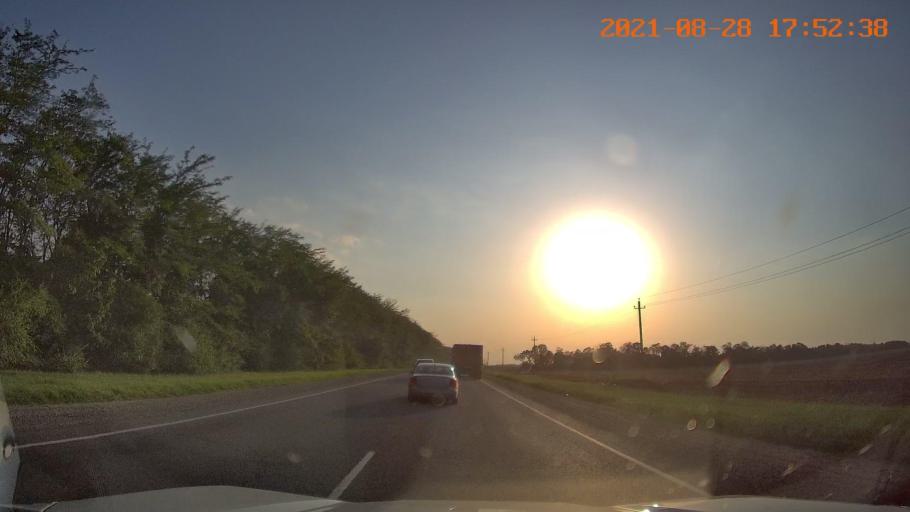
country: RU
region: Krasnodarskiy
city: Konstantinovskaya
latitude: 44.9403
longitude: 40.7735
